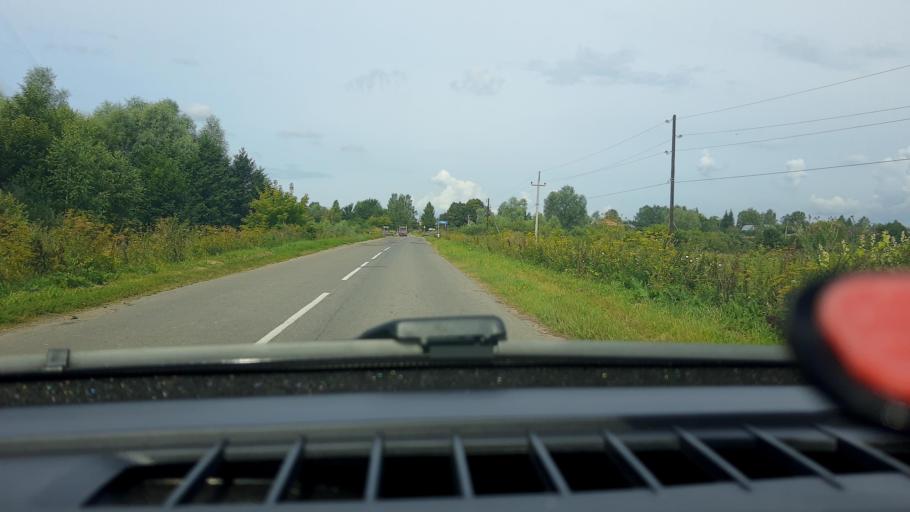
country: RU
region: Nizjnij Novgorod
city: Burevestnik
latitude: 56.0647
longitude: 43.6689
